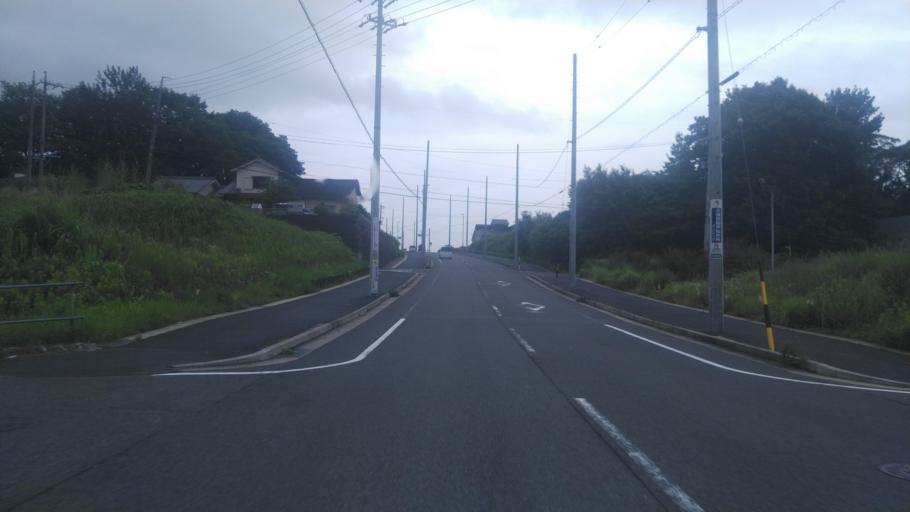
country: JP
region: Aichi
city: Kasugai
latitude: 35.2508
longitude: 137.0214
